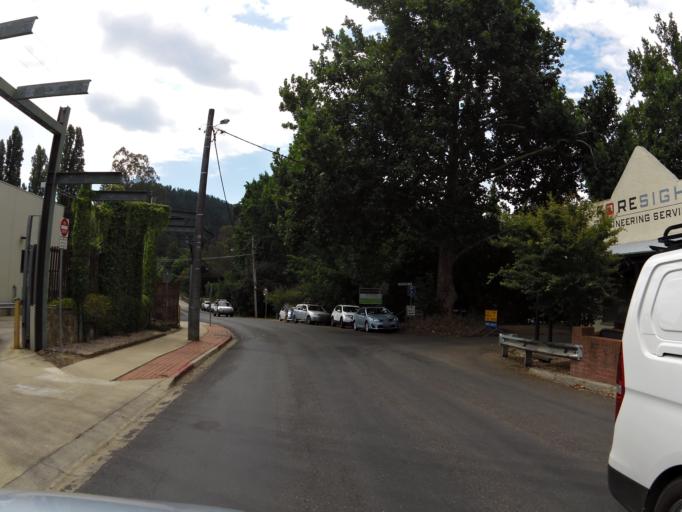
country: AU
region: Victoria
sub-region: Alpine
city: Mount Beauty
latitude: -36.7271
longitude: 146.9593
